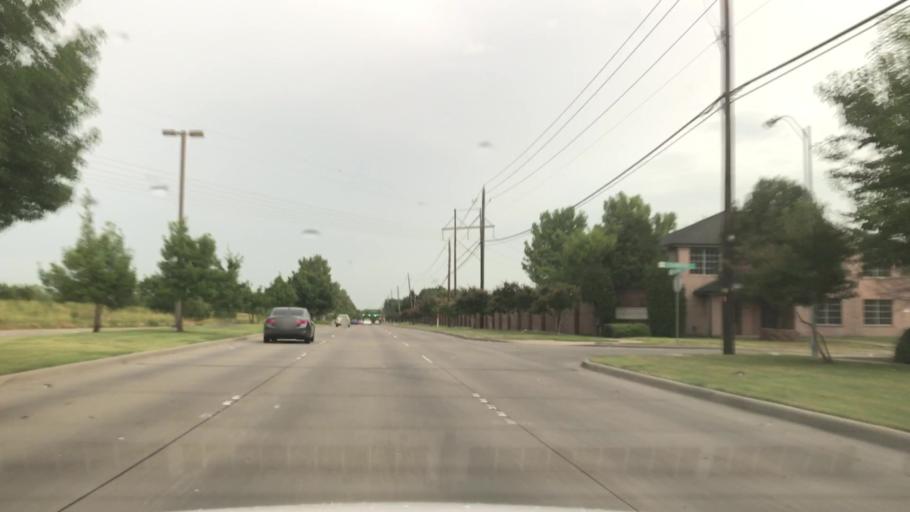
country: US
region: Texas
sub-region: Dallas County
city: Mesquite
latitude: 32.7421
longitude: -96.5770
